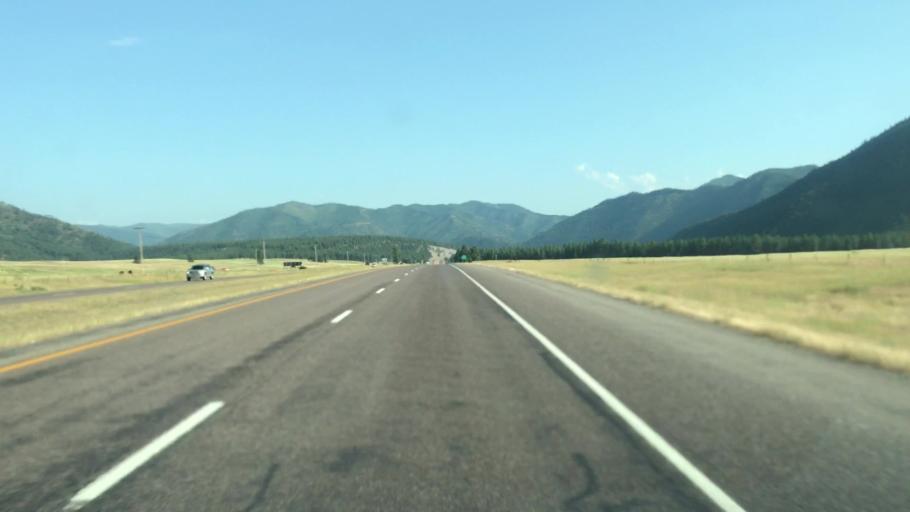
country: US
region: Montana
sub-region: Mineral County
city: Superior
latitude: 47.0465
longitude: -114.7535
